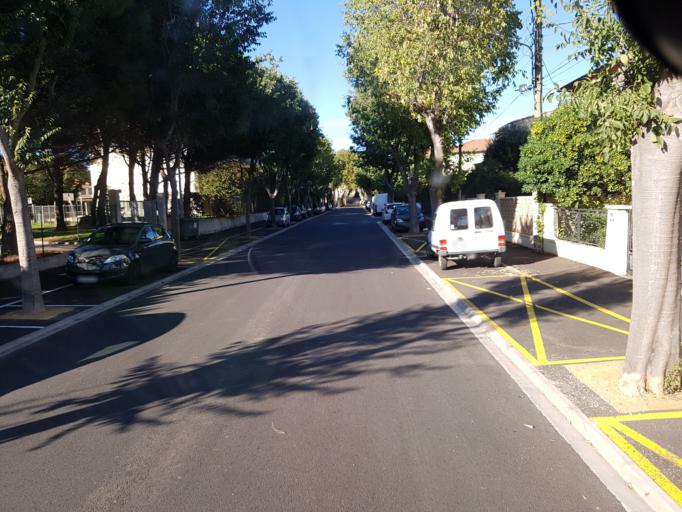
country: FR
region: Languedoc-Roussillon
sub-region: Departement de l'Aude
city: Narbonne
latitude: 43.1765
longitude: 3.0035
